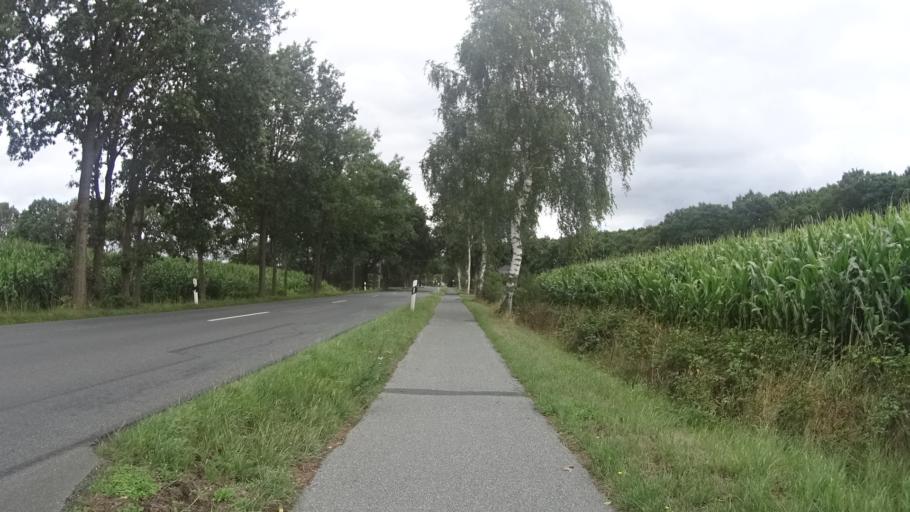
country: DE
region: Lower Saxony
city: Schiffdorf
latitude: 53.5428
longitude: 8.6801
